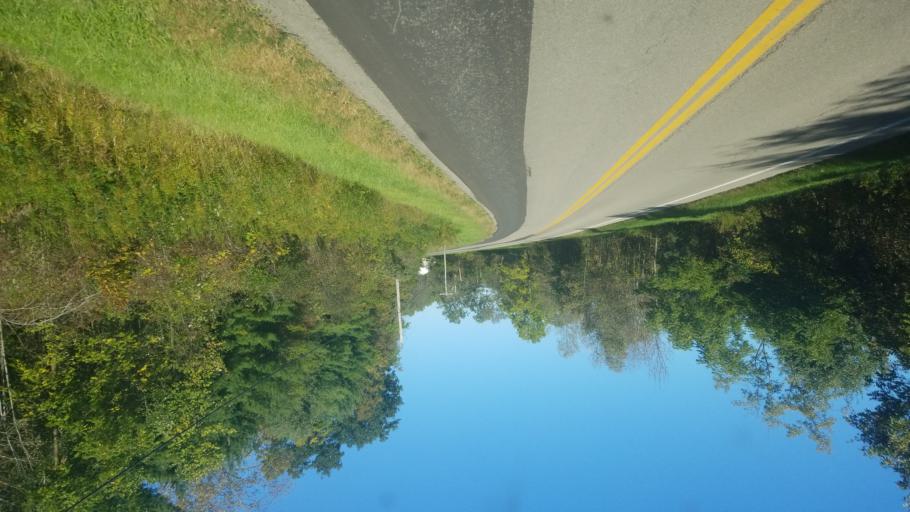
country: US
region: New York
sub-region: Allegany County
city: Friendship
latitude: 42.2954
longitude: -78.1174
